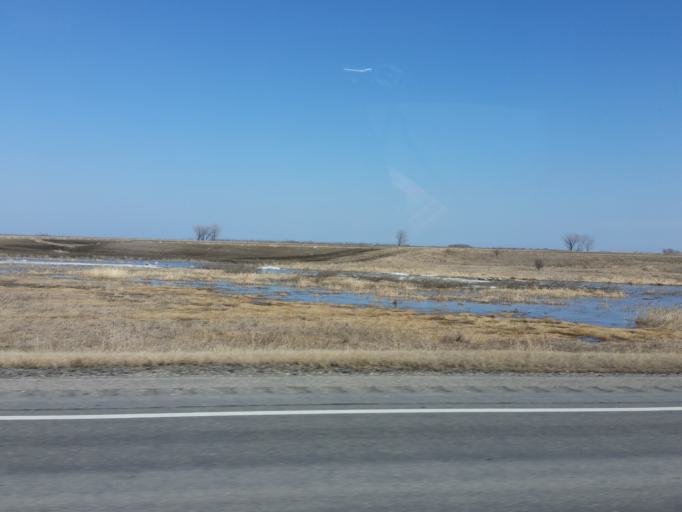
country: US
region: North Dakota
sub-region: Walsh County
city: Grafton
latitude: 48.1937
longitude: -97.3271
